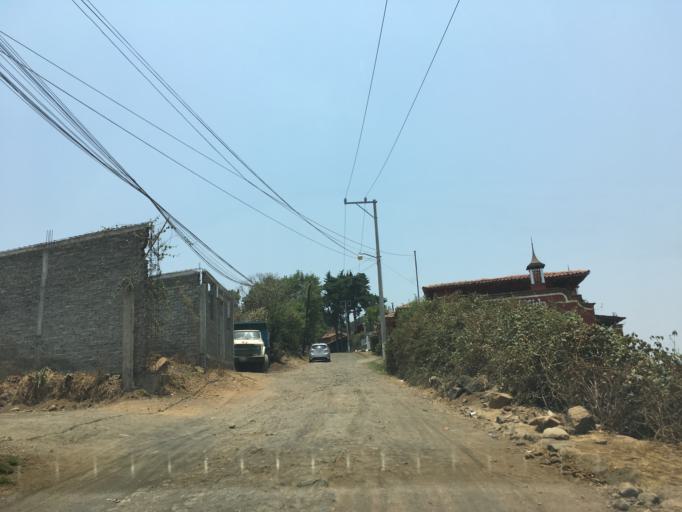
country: MX
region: Michoacan
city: Patzcuaro
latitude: 19.5155
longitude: -101.6224
